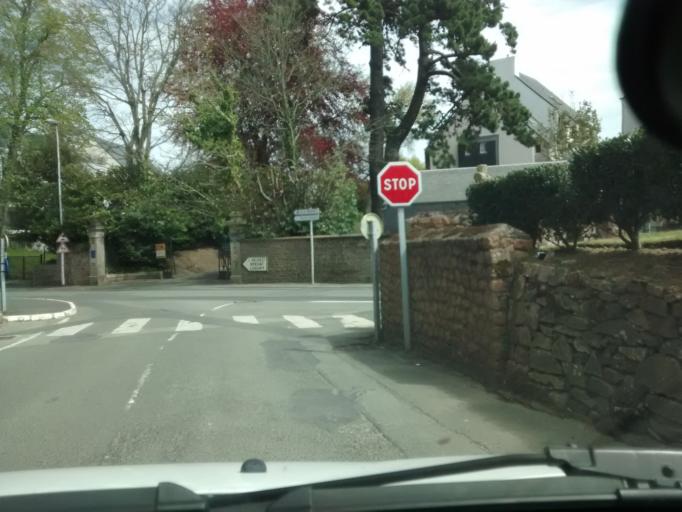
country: FR
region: Brittany
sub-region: Departement des Cotes-d'Armor
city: Paimpol
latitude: 48.7805
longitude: -3.0497
